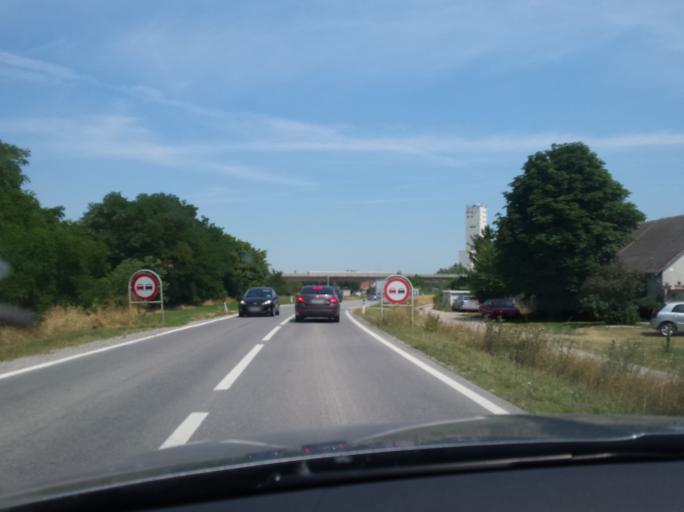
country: AT
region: Lower Austria
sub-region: Politischer Bezirk Bruck an der Leitha
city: Petronell-Carnuntum
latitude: 48.1025
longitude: 16.8640
